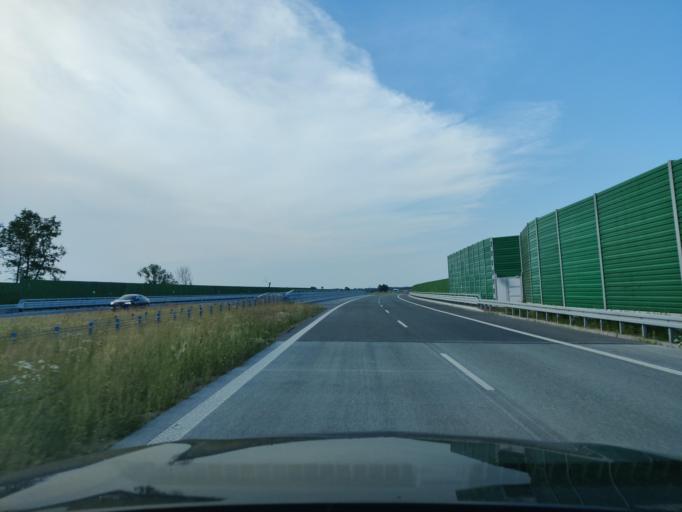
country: PL
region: Masovian Voivodeship
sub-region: Powiat mlawski
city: Strzegowo
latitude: 52.8944
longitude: 20.2635
